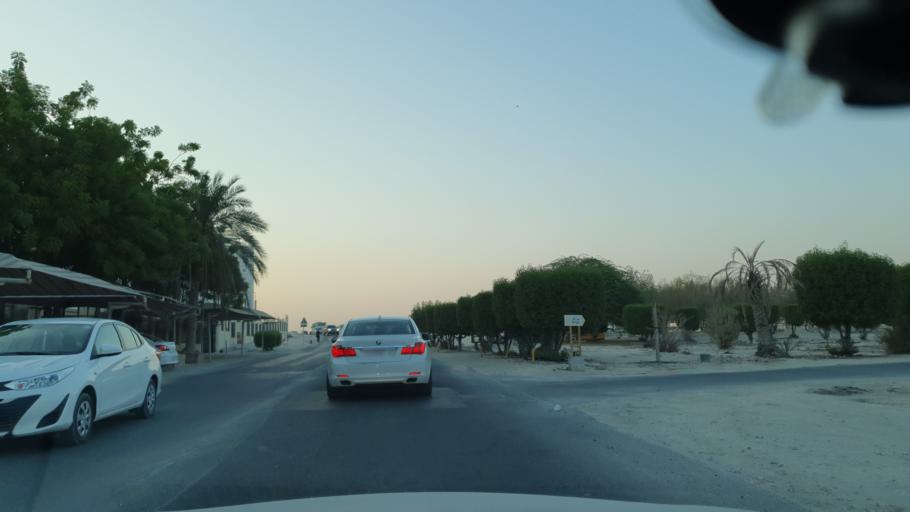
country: BH
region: Northern
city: Ar Rifa'
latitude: 26.1520
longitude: 50.5713
